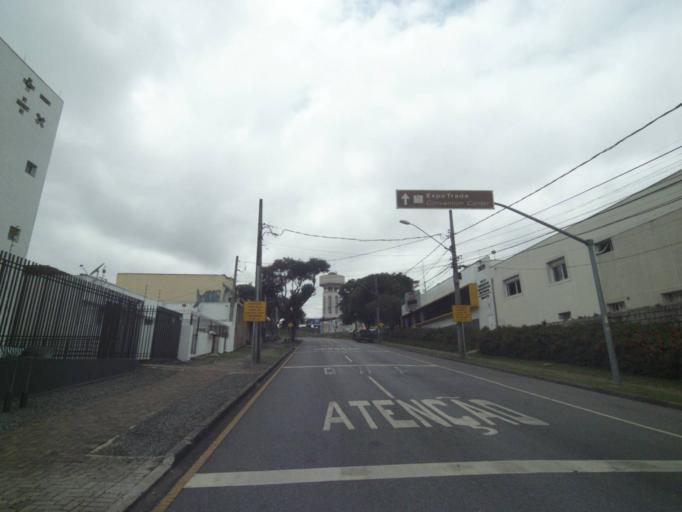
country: BR
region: Parana
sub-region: Curitiba
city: Curitiba
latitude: -25.4282
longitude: -49.2435
